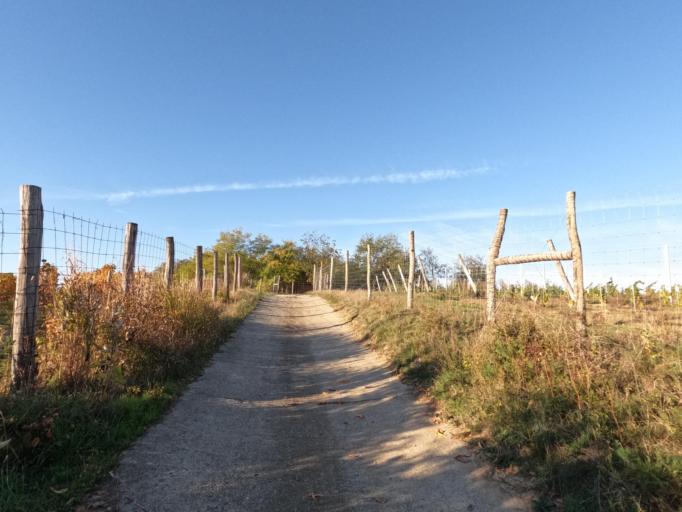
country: HU
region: Tolna
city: Szekszard
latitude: 46.3077
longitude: 18.6599
